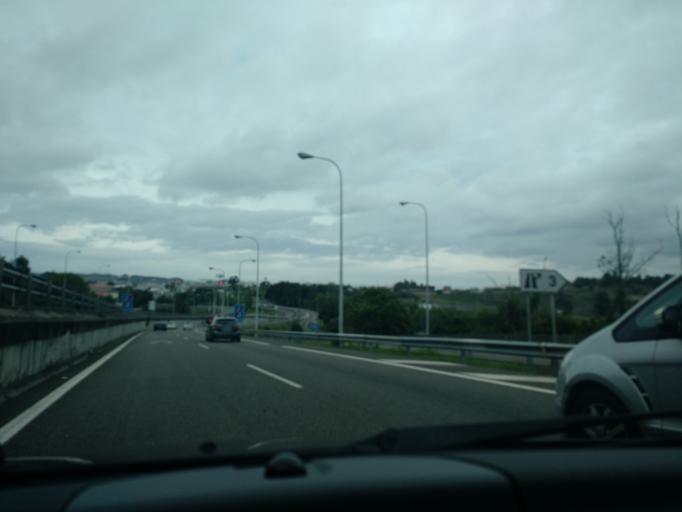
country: ES
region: Galicia
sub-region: Provincia da Coruna
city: Culleredo
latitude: 43.3266
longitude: -8.3950
